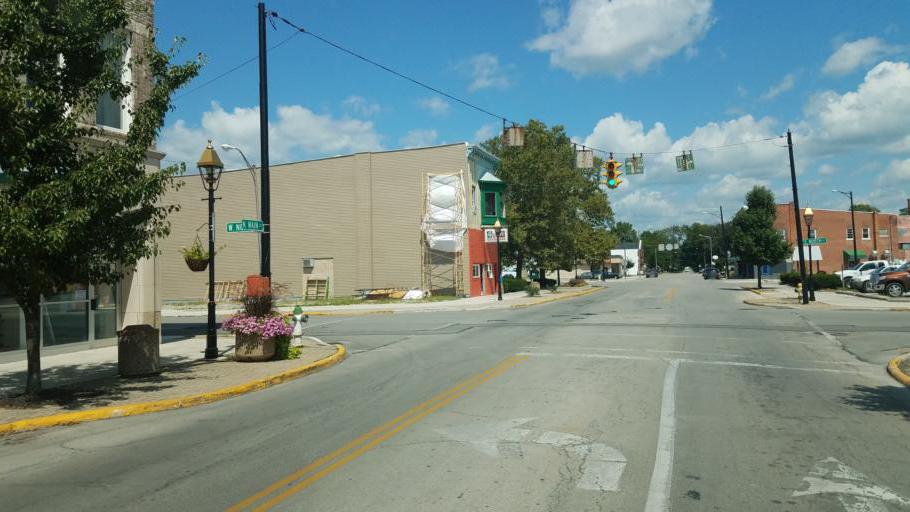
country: US
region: Ohio
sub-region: Seneca County
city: Fostoria
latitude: 41.1580
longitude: -83.4141
